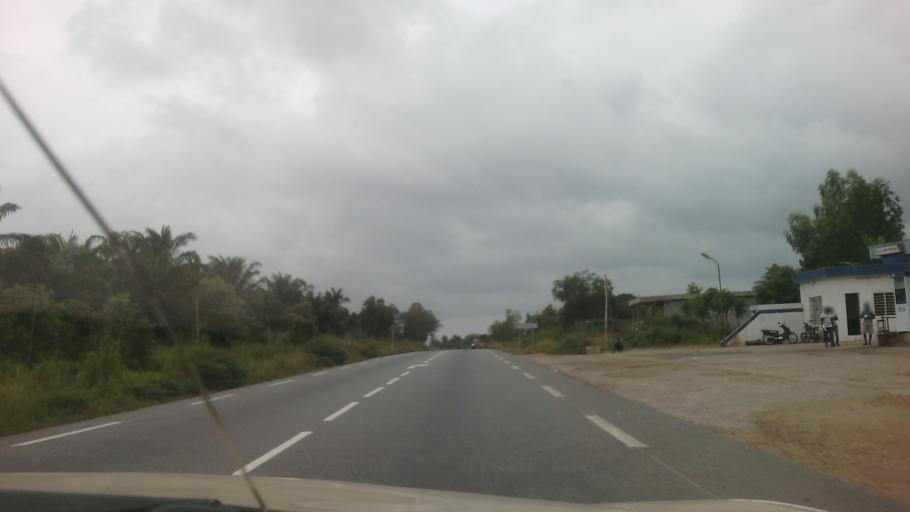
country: BJ
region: Mono
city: Come
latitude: 6.3972
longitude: 1.9797
